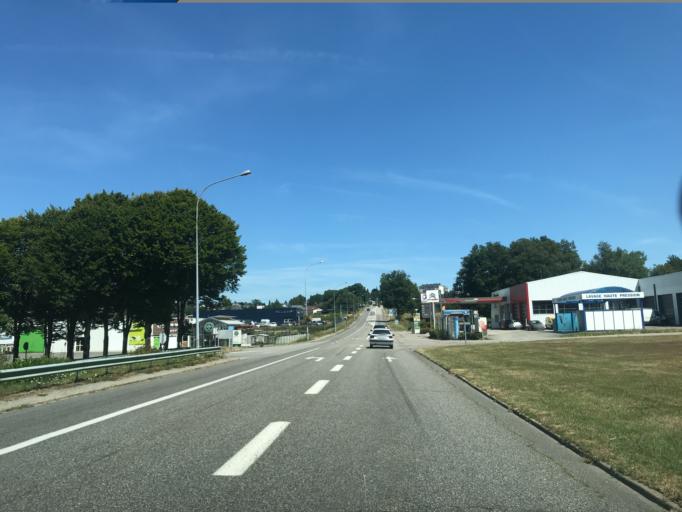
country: FR
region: Limousin
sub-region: Departement de la Correze
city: Egletons
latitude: 45.3976
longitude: 2.0349
